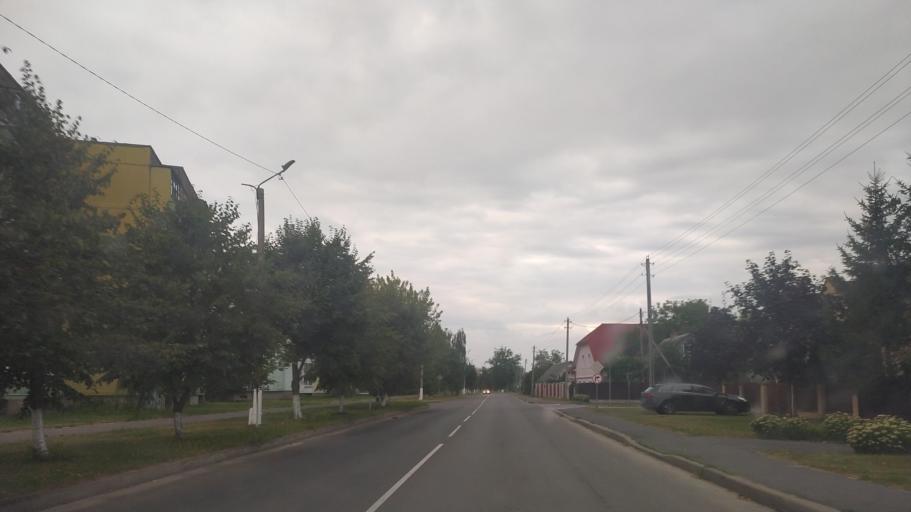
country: BY
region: Brest
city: Byaroza
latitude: 52.5284
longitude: 24.9881
